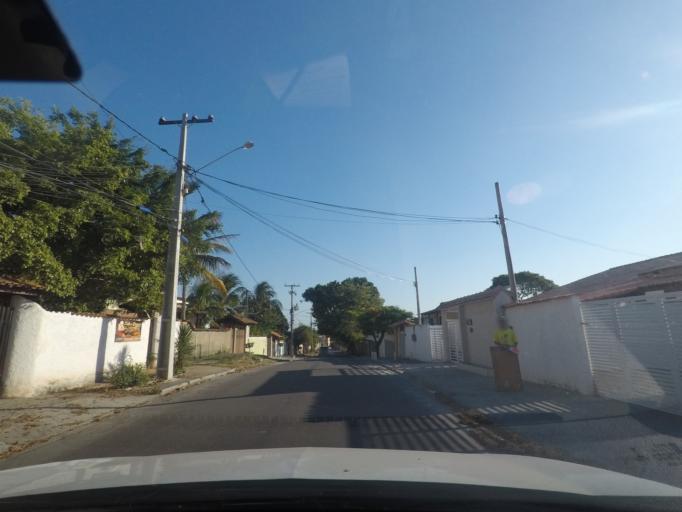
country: BR
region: Rio de Janeiro
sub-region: Marica
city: Marica
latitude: -22.9679
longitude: -42.9378
